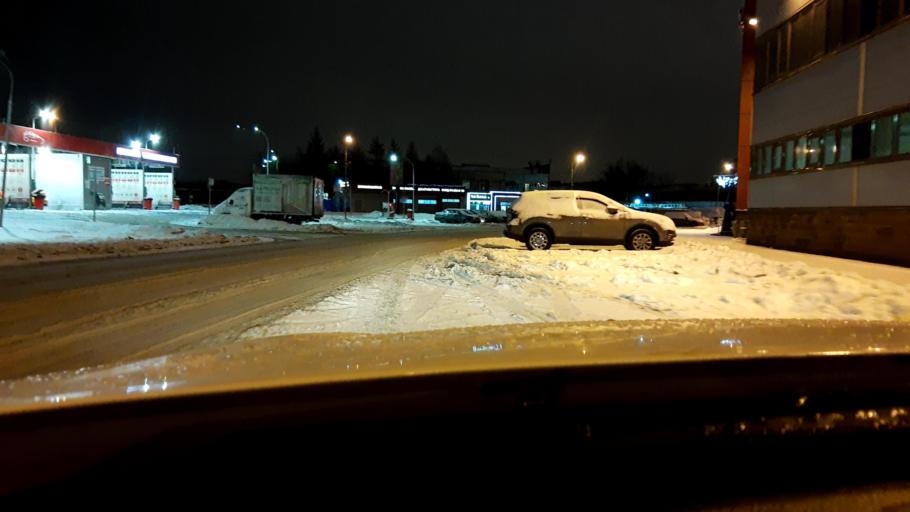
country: RU
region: Moscow
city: Khimki
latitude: 55.9127
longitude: 37.4184
